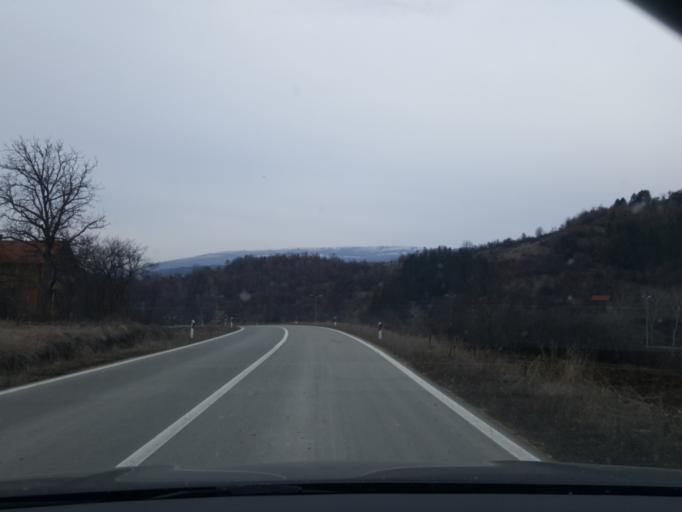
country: RS
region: Central Serbia
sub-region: Pirotski Okrug
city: Pirot
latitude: 43.1926
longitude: 22.5614
